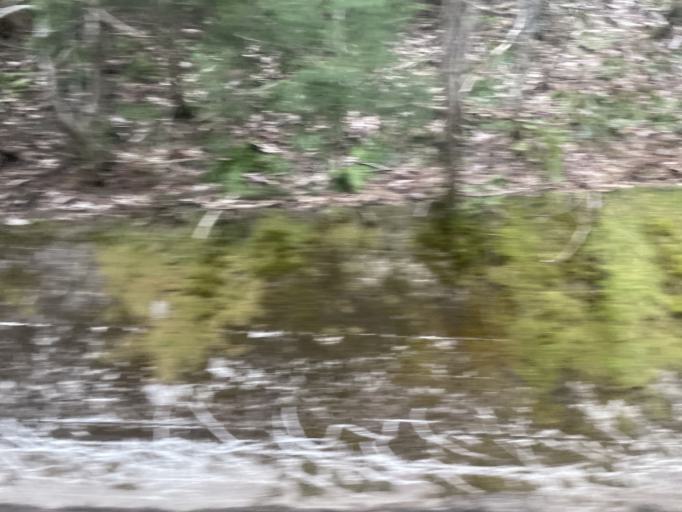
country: JP
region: Akita
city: Kakunodatemachi
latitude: 39.7000
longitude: 140.5552
